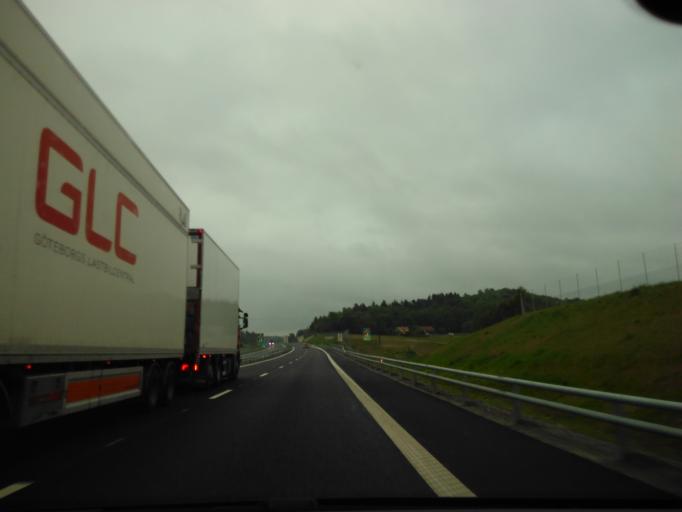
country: SE
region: Vaestra Goetaland
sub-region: Alingsas Kommun
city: Alingsas
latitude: 57.9375
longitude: 12.5821
